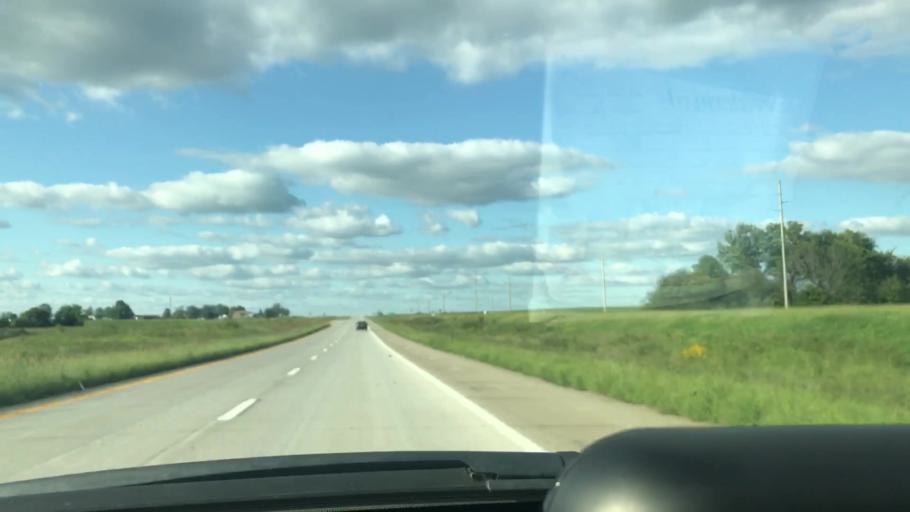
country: US
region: Missouri
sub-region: Benton County
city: Cole Camp
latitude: 38.4952
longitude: -93.2734
